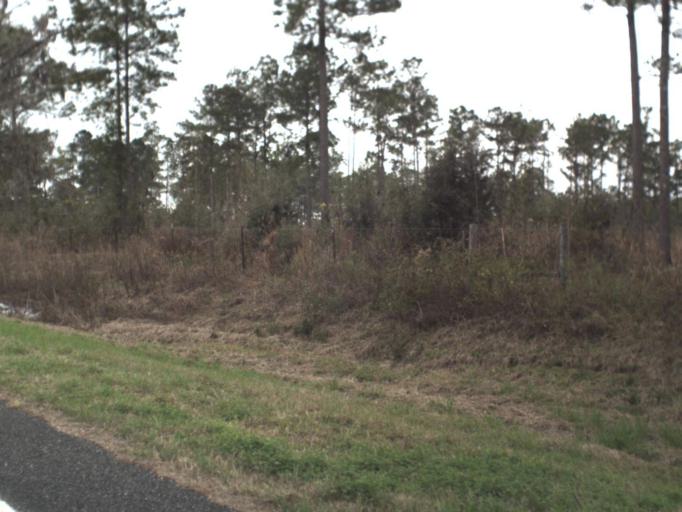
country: US
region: Florida
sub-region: Jefferson County
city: Monticello
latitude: 30.4049
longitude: -84.0187
